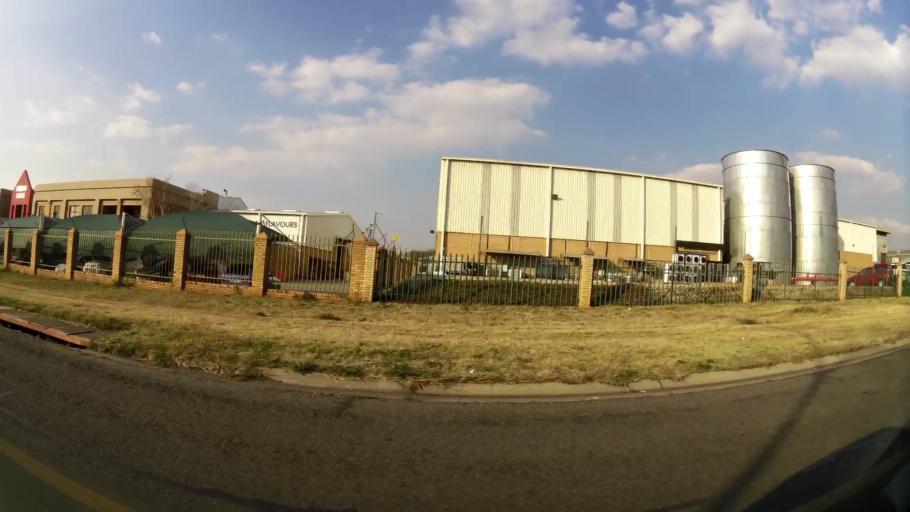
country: ZA
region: Gauteng
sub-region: City of Johannesburg Metropolitan Municipality
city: Modderfontein
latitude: -26.1199
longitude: 28.2003
